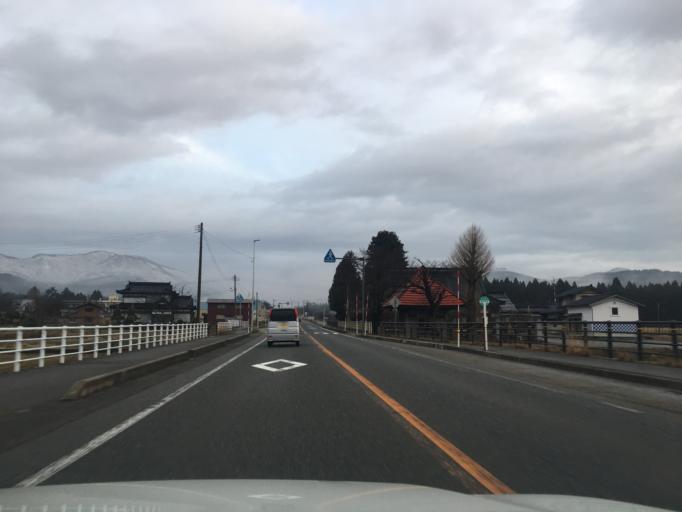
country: JP
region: Niigata
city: Murakami
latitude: 38.3288
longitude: 139.5555
